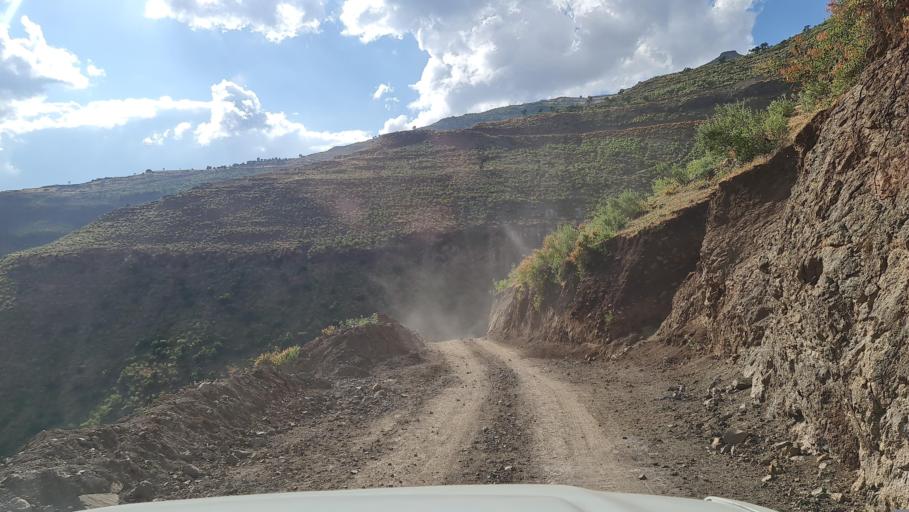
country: ET
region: Amhara
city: Debark'
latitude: 13.1186
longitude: 38.0208
